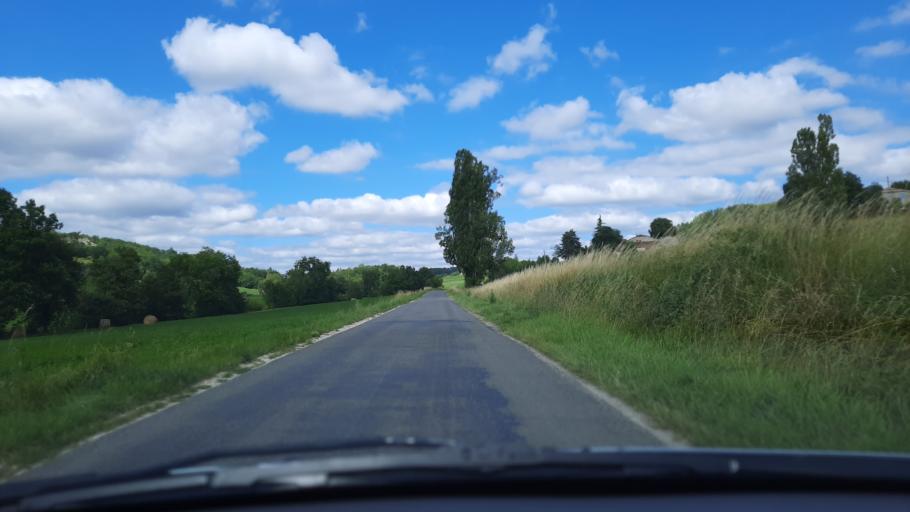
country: FR
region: Midi-Pyrenees
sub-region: Departement du Lot
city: Castelnau-Montratier
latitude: 44.2874
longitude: 1.4241
